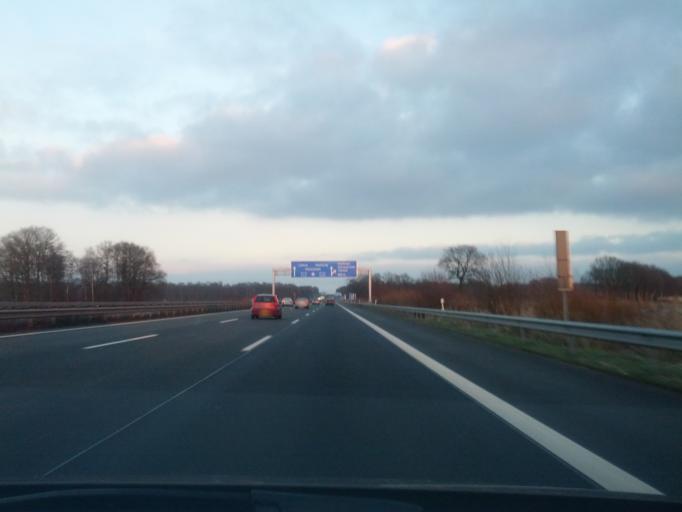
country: DE
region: Lower Saxony
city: Halvesbostel
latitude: 53.3333
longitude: 9.6197
